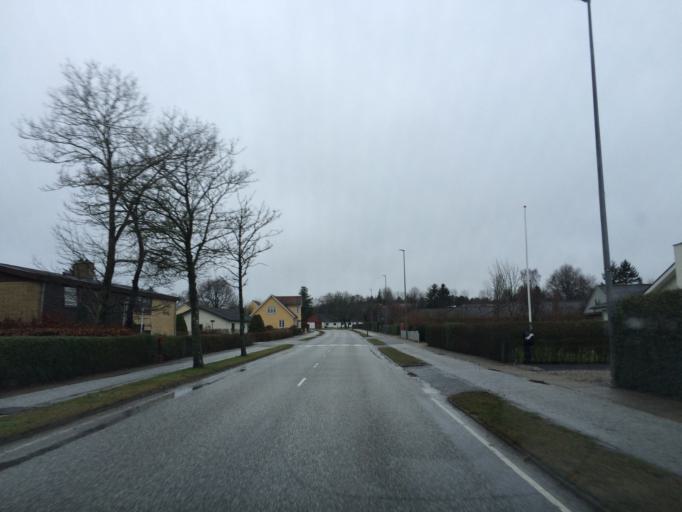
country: DK
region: North Denmark
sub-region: Rebild Kommune
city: Skorping
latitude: 56.8345
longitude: 9.8519
